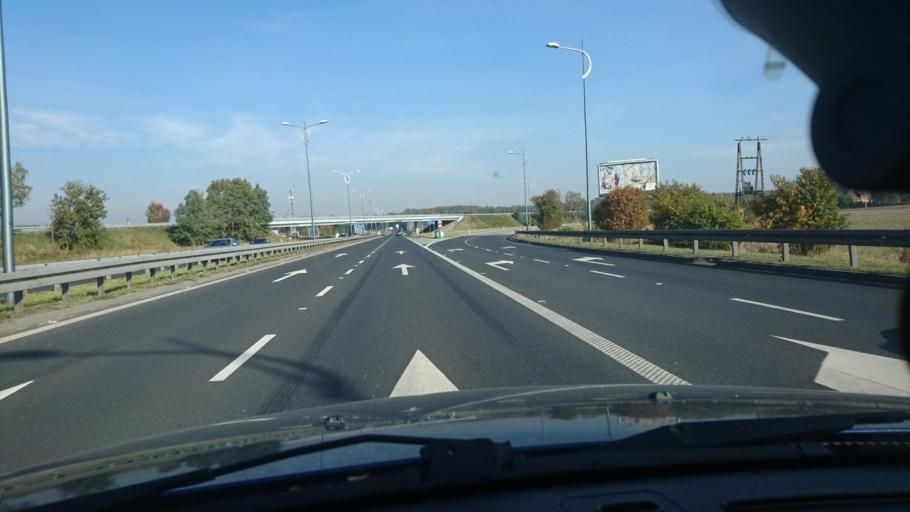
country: PL
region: Silesian Voivodeship
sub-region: Tychy
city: Cielmice
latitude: 50.1318
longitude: 19.0252
